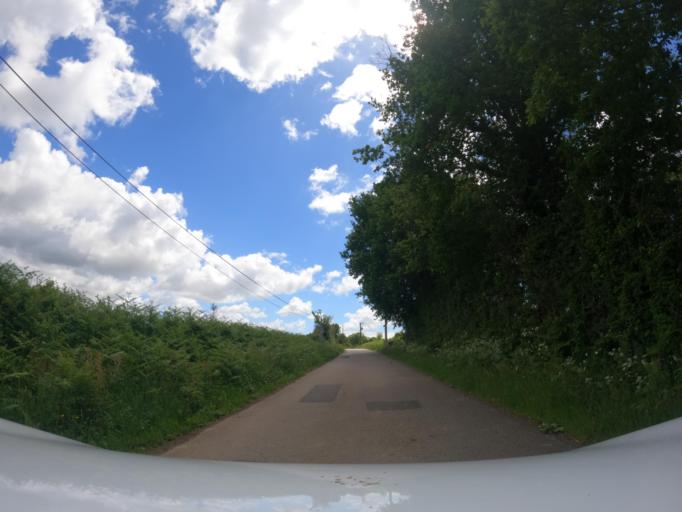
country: FR
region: Pays de la Loire
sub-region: Departement de la Vendee
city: Le Champ-Saint-Pere
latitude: 46.4925
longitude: -1.3572
